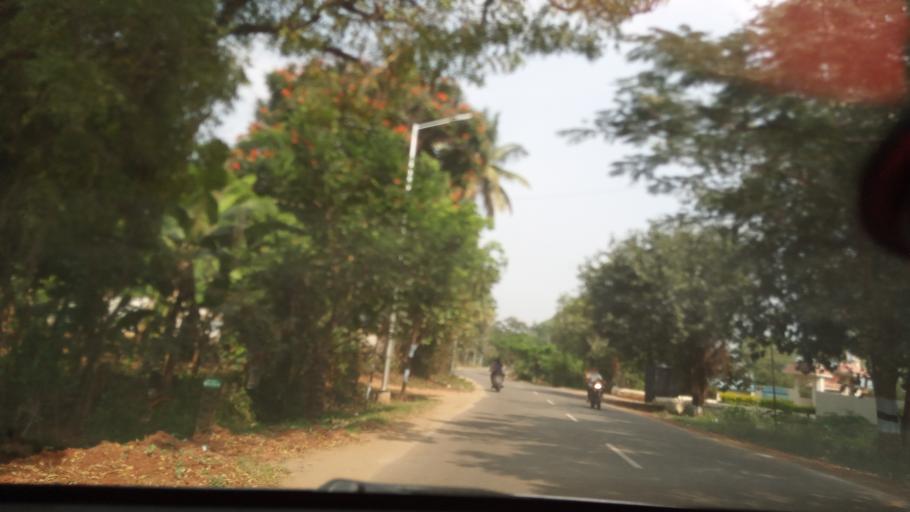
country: IN
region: Tamil Nadu
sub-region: Coimbatore
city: Perur
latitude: 11.0104
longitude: 76.8708
